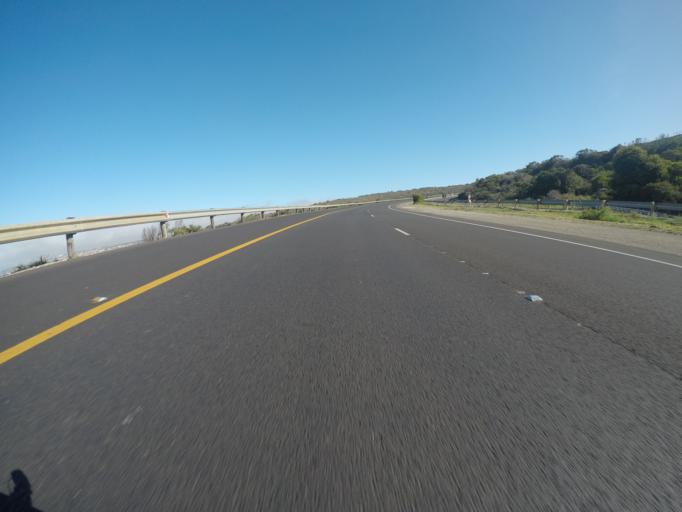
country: ZA
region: Western Cape
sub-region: Eden District Municipality
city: Mossel Bay
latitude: -34.1575
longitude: 22.0997
